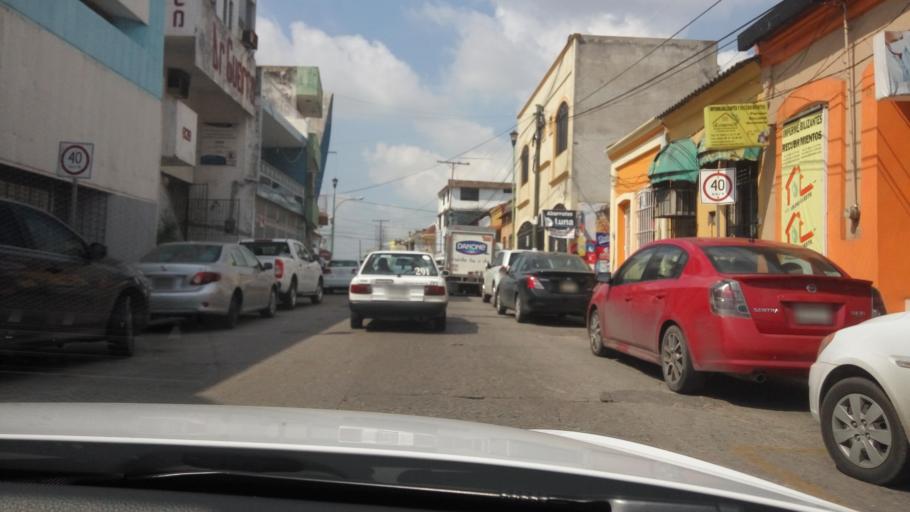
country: MX
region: Tabasco
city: Villahermosa
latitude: 17.9907
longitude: -92.9219
